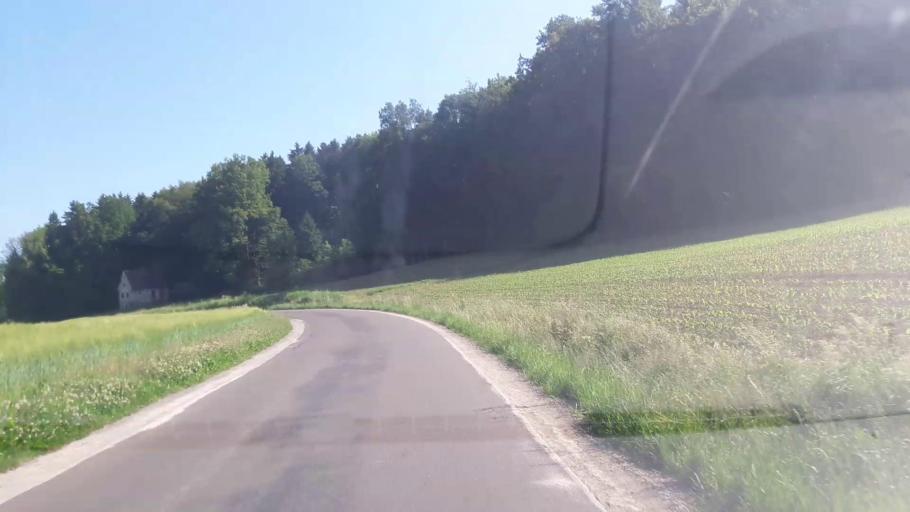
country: AT
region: Styria
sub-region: Politischer Bezirk Hartberg-Fuerstenfeld
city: UEbersbach
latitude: 46.9940
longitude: 16.0448
